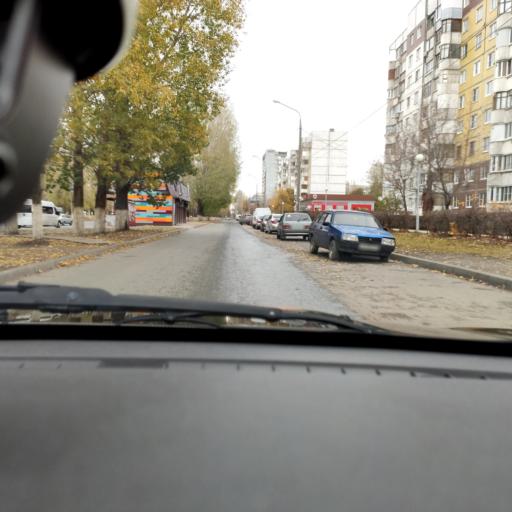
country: RU
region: Samara
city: Tol'yatti
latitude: 53.5367
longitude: 49.3447
